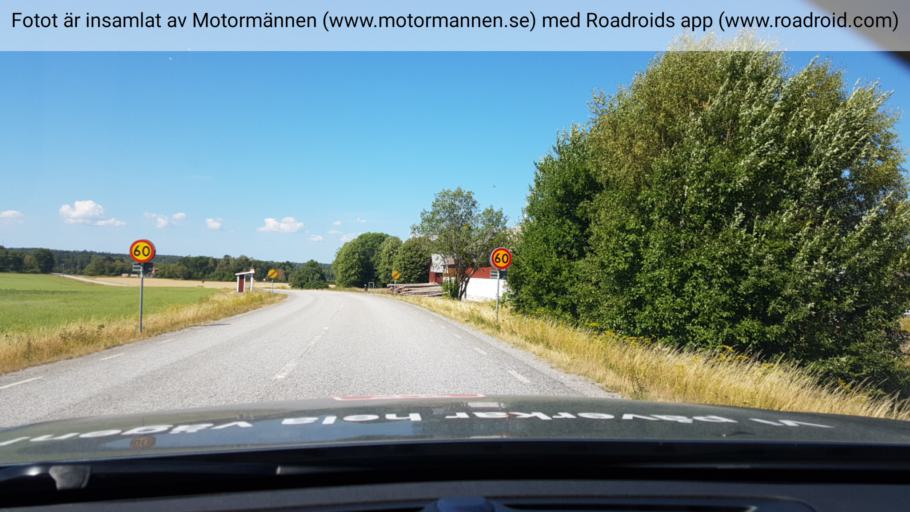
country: SE
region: Stockholm
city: Stenhamra
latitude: 59.3984
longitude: 17.5546
